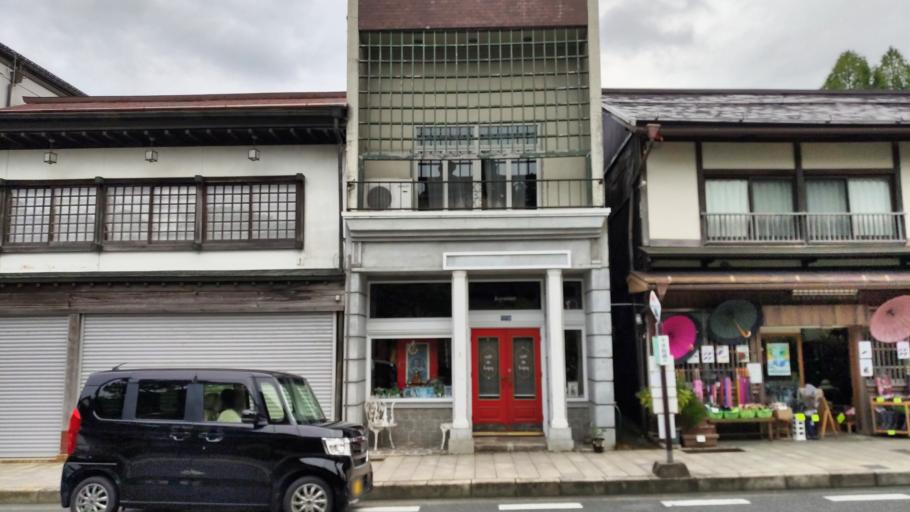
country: JP
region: Wakayama
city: Koya
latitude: 34.2132
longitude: 135.5859
